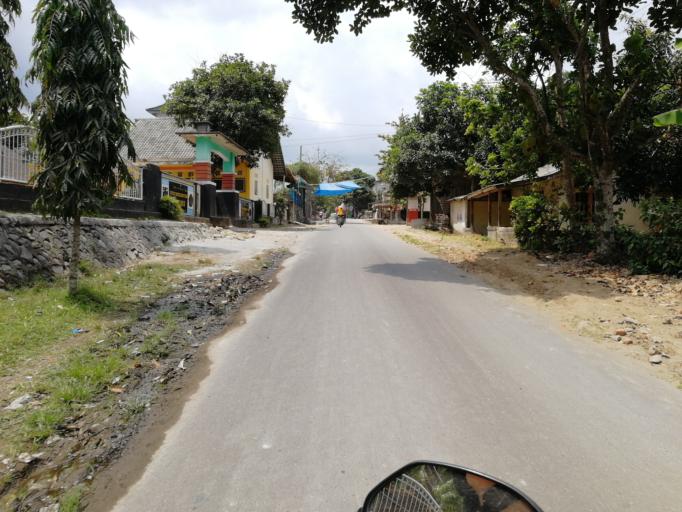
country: ID
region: West Nusa Tenggara
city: Pediti
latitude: -8.5620
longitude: 116.3319
